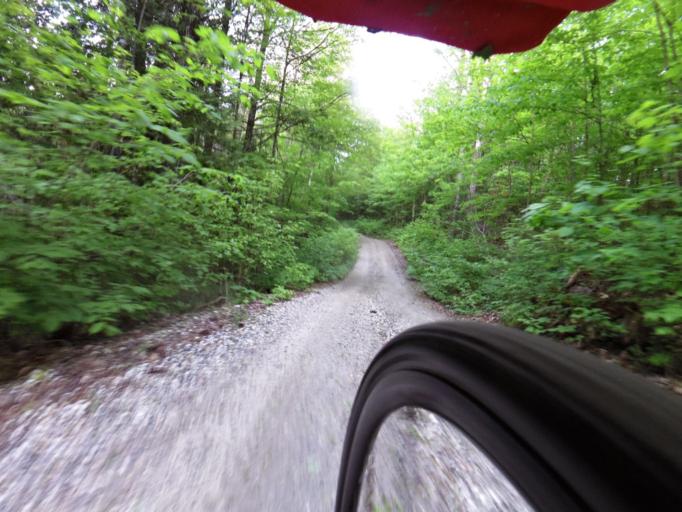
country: CA
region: Ontario
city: Arnprior
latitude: 45.1778
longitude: -76.5199
